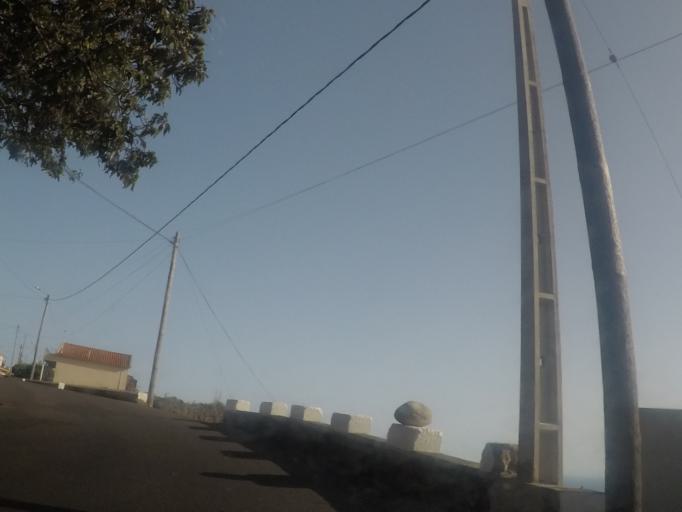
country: PT
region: Madeira
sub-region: Calheta
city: Arco da Calheta
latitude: 32.7049
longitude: -17.1264
